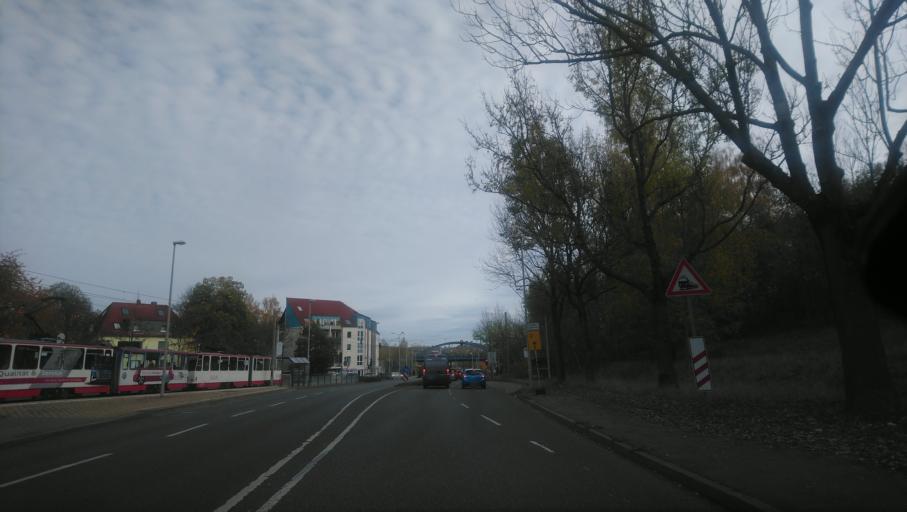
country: DE
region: Saxony
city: Zwickau
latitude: 50.7025
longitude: 12.4902
